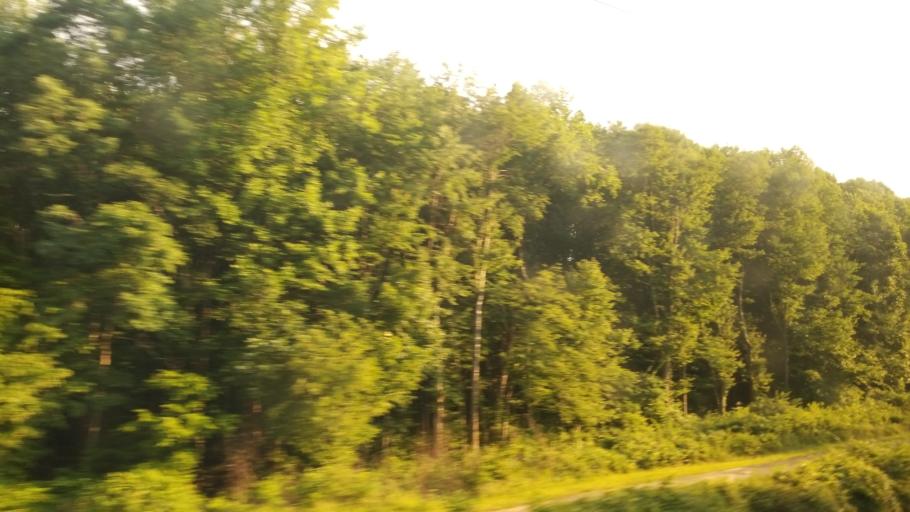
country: US
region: Virginia
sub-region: Fairfax County
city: Burke
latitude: 38.7981
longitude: -77.2854
